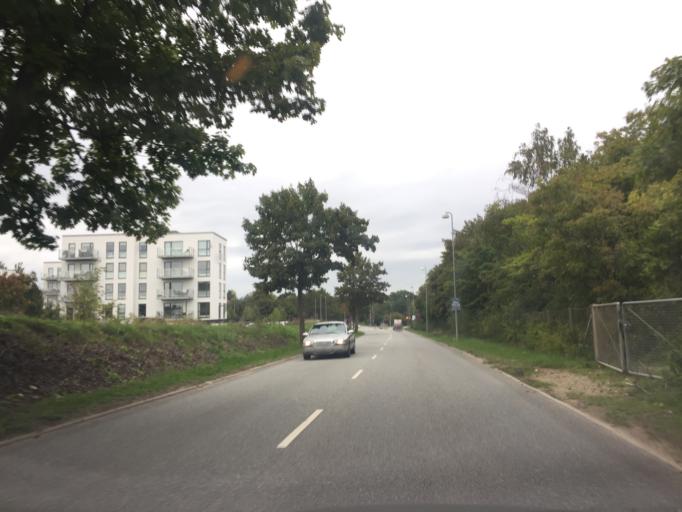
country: DK
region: Capital Region
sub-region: Hillerod Kommune
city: Hillerod
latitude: 55.9402
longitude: 12.2640
